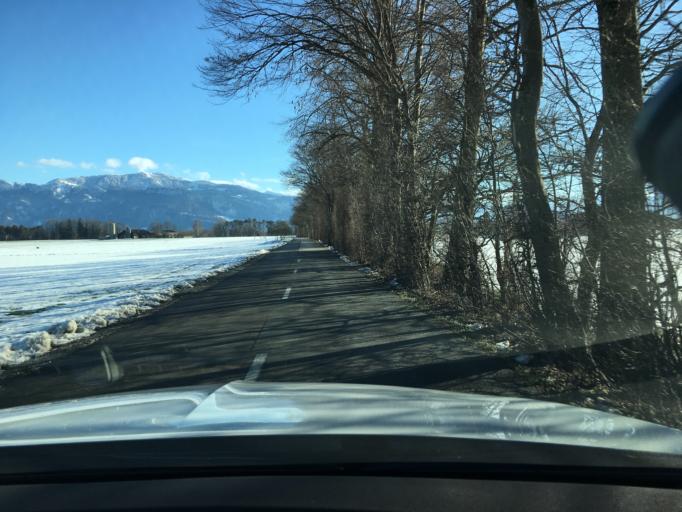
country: CH
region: Saint Gallen
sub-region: Wahlkreis Rheintal
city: Rebstein
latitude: 47.3850
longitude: 9.5805
